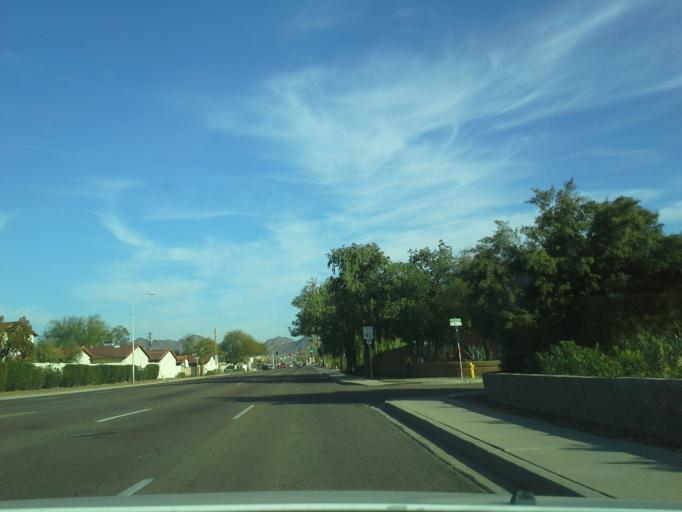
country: US
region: Arizona
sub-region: Maricopa County
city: Glendale
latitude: 33.5675
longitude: -112.0856
